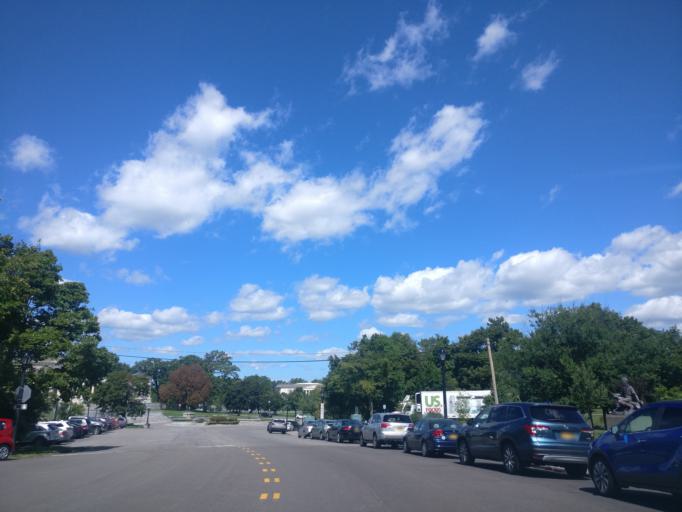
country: US
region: New York
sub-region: Erie County
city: Kenmore
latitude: 42.9314
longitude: -78.8738
